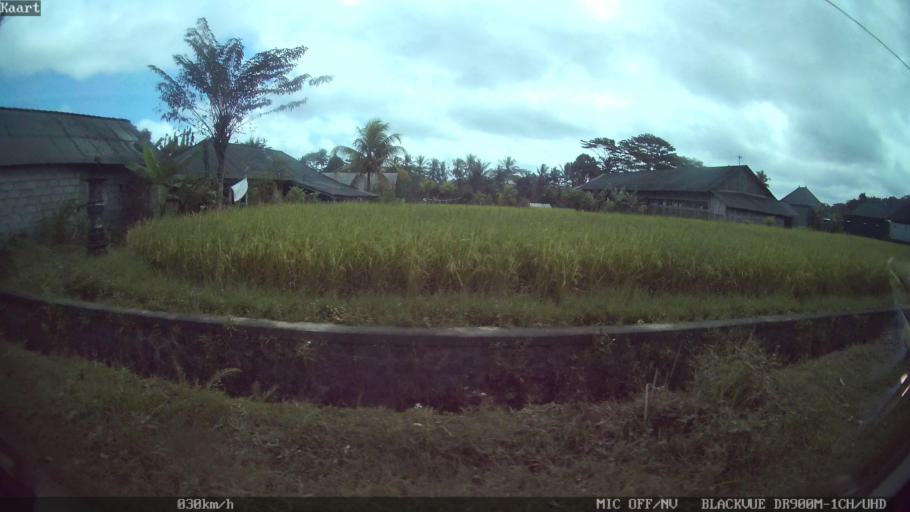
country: ID
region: Bali
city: Banjar Abuan
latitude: -8.4595
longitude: 115.3396
